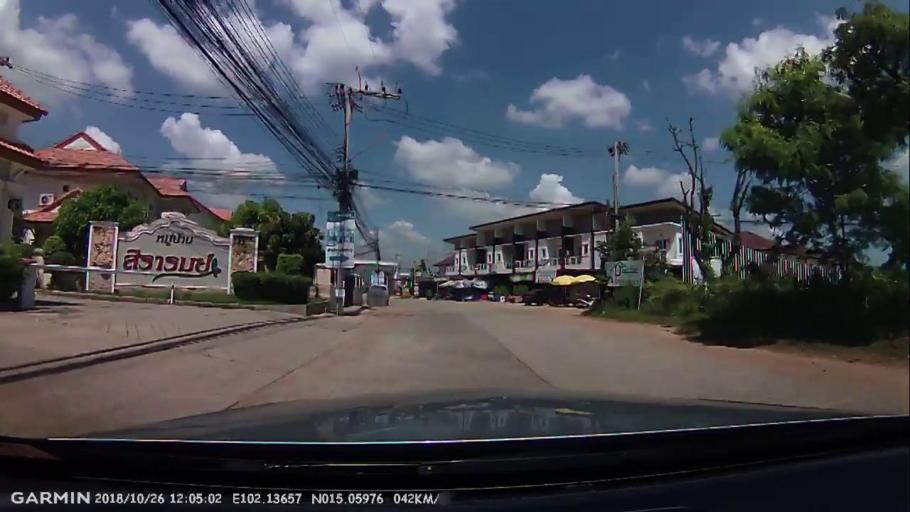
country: TH
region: Nakhon Ratchasima
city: Nakhon Ratchasima
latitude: 15.0598
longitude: 102.1366
